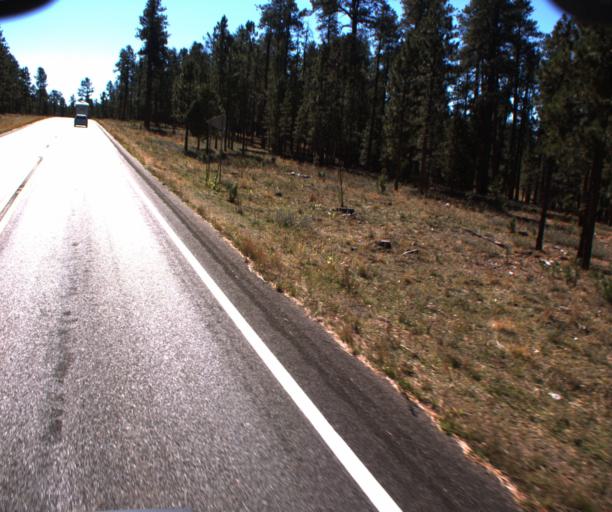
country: US
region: Arizona
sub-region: Coconino County
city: Fredonia
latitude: 36.6751
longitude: -112.2090
